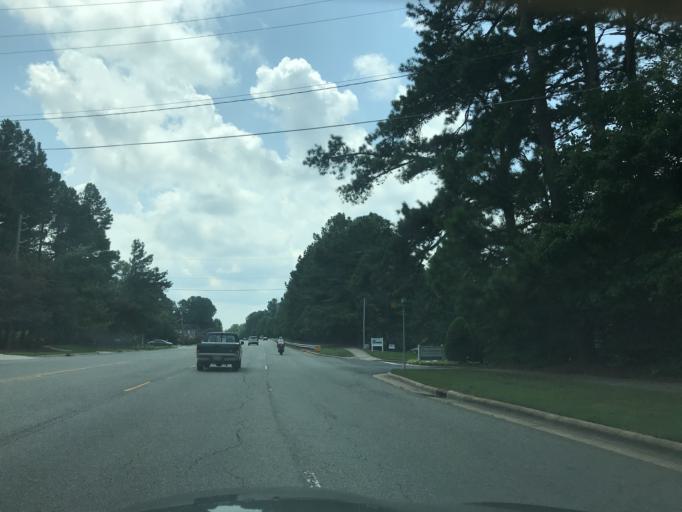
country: US
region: North Carolina
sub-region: Wake County
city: West Raleigh
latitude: 35.8542
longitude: -78.7114
